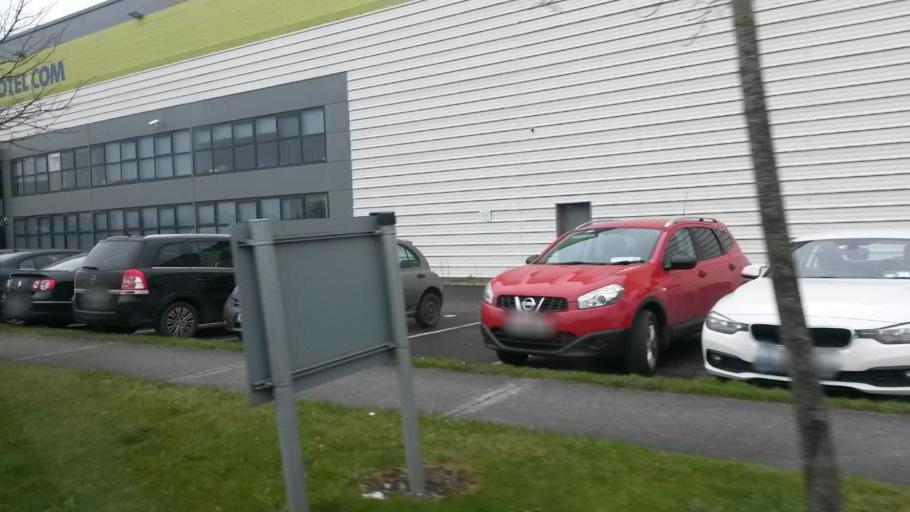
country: IE
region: Leinster
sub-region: Dublin City
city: Finglas
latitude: 53.3990
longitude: -6.3198
